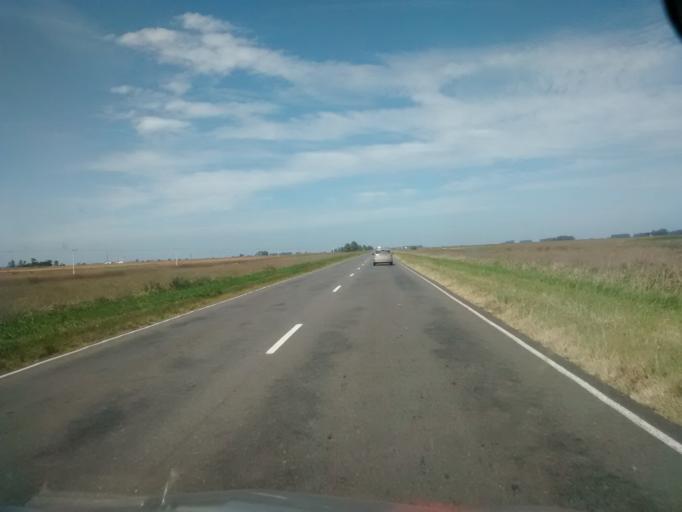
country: AR
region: Buenos Aires
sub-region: Partido de Ayacucho
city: Ayacucho
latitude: -36.6761
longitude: -58.5749
